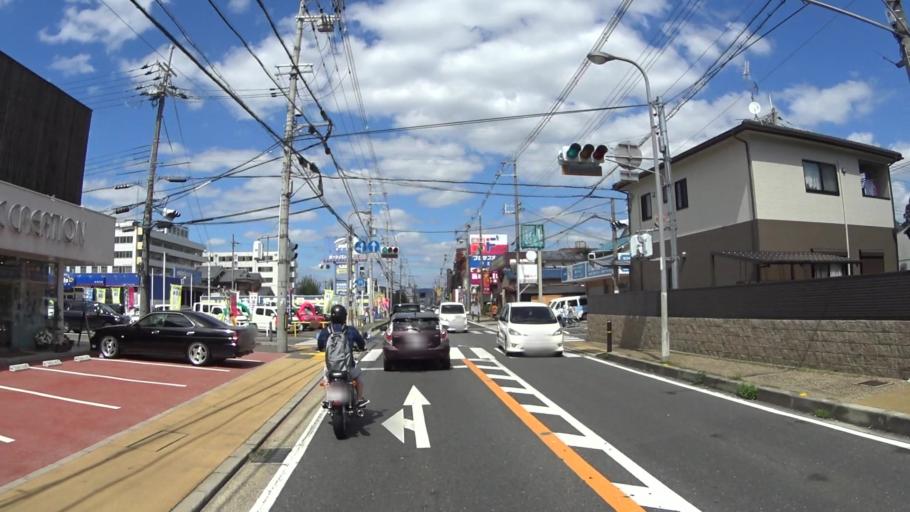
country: JP
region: Kyoto
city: Uji
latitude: 34.8975
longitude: 135.7834
